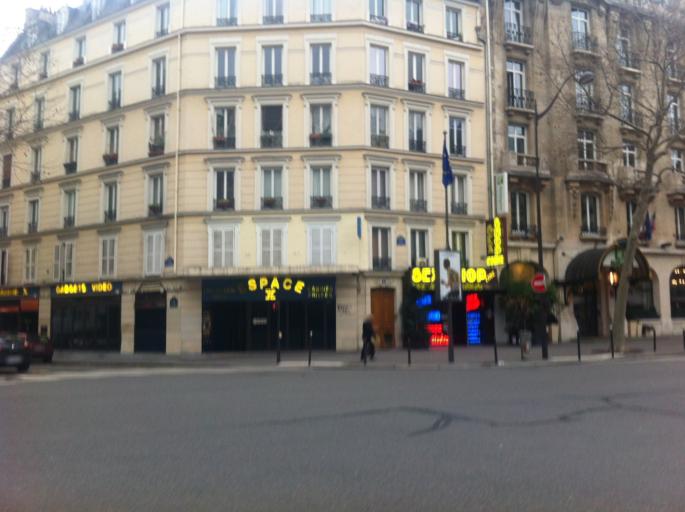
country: FR
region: Ile-de-France
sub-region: Paris
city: Paris
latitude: 48.8466
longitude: 2.3723
